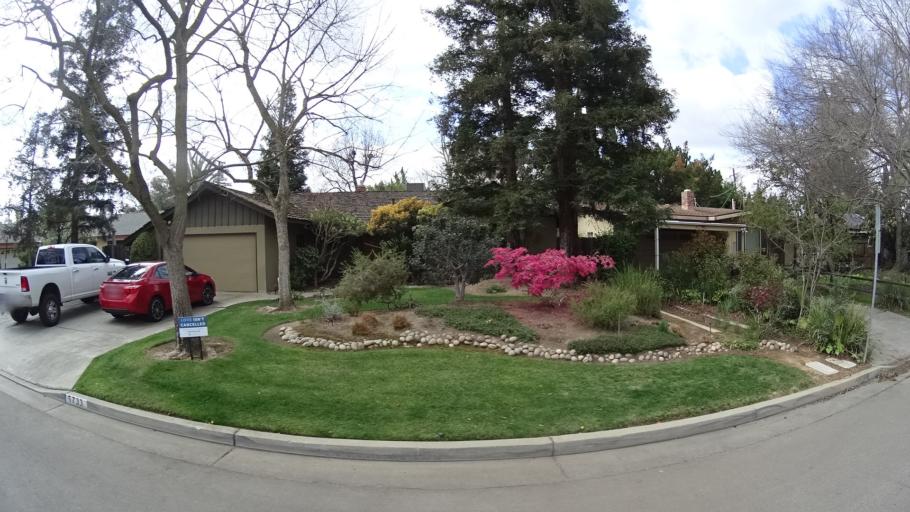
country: US
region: California
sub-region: Fresno County
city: Clovis
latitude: 36.8221
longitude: -119.7649
